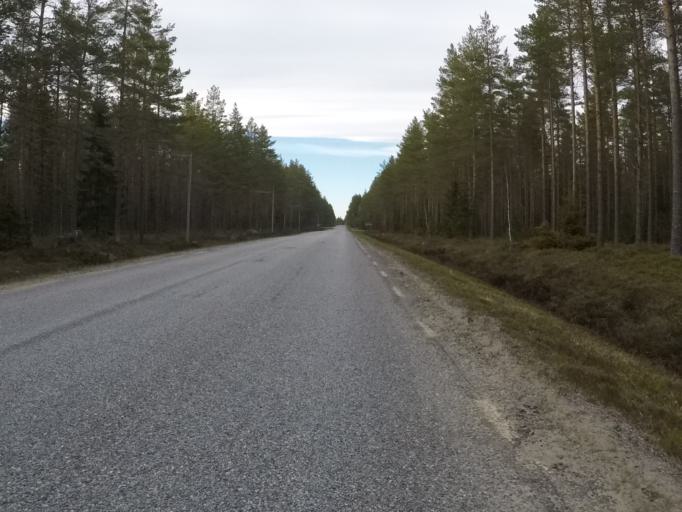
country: SE
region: Vaesterbotten
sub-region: Umea Kommun
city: Saevar
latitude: 63.9314
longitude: 20.7805
